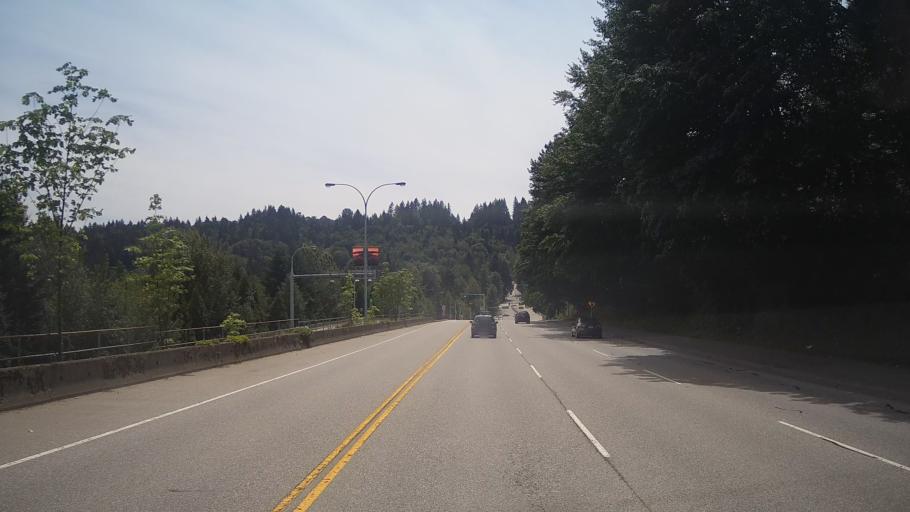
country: CA
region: British Columbia
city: Port Moody
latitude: 49.2821
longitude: -122.8670
